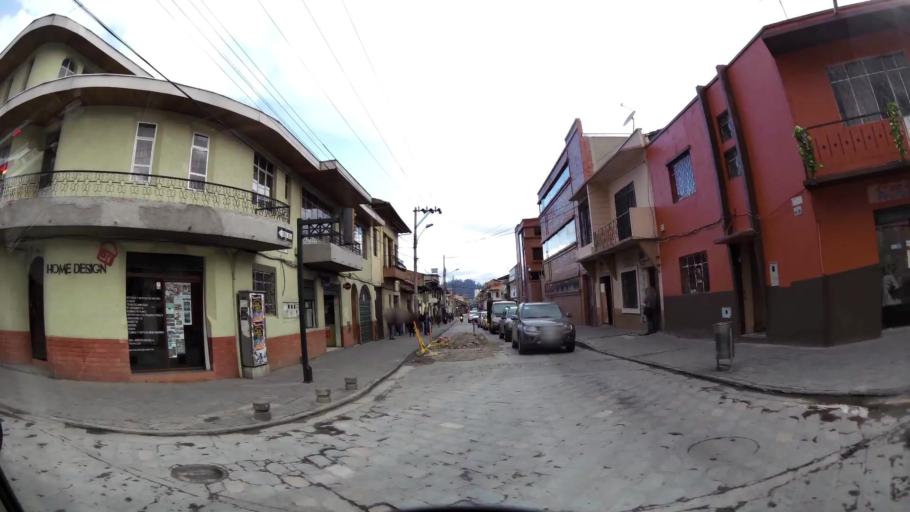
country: EC
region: Azuay
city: Cuenca
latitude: -2.8910
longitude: -79.0069
